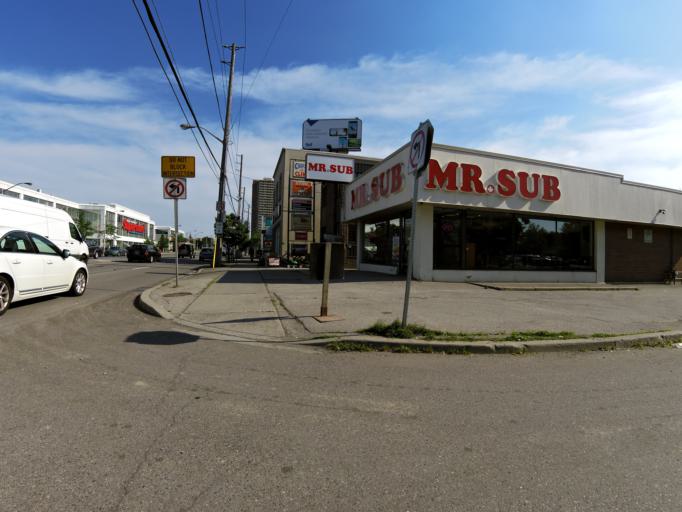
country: CA
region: Ontario
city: Etobicoke
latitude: 43.7112
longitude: -79.5353
